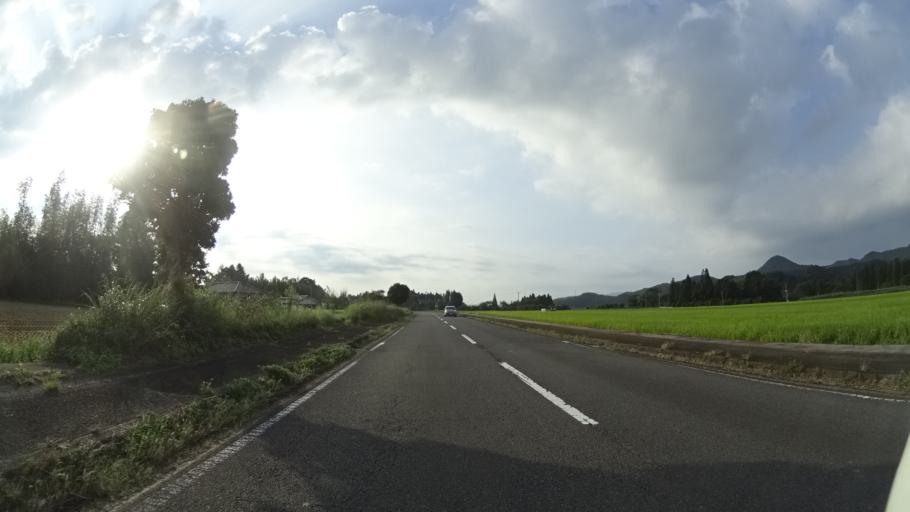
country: JP
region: Kagoshima
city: Okuchi-shinohara
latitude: 32.0917
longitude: 130.5853
